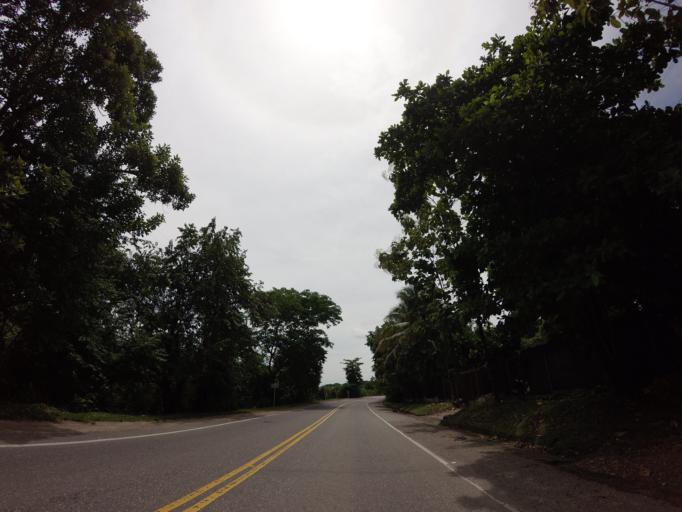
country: CO
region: Caldas
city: La Dorada
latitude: 5.4201
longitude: -74.6859
